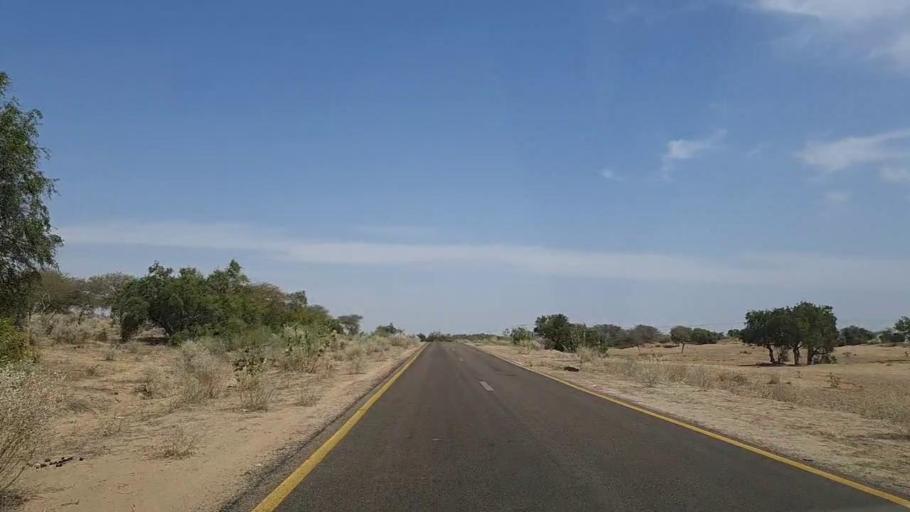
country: PK
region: Sindh
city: Mithi
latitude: 24.8841
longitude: 69.8721
